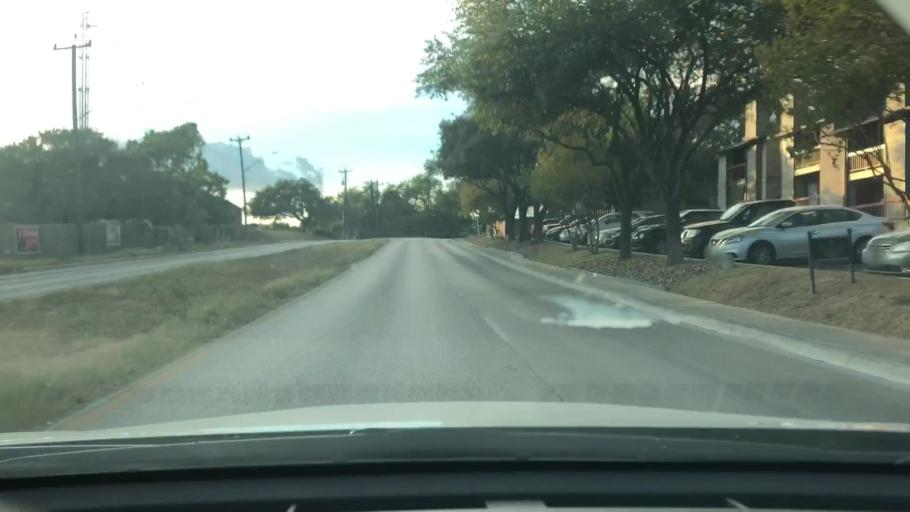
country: US
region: Texas
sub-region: Bexar County
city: Hollywood Park
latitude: 29.5547
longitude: -98.4706
